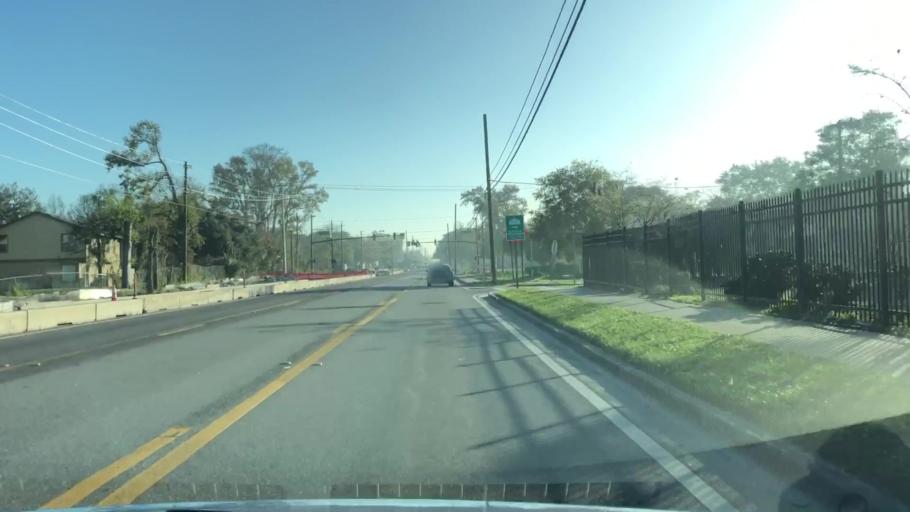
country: US
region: Florida
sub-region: Seminole County
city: Sanford
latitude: 28.7866
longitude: -81.2816
